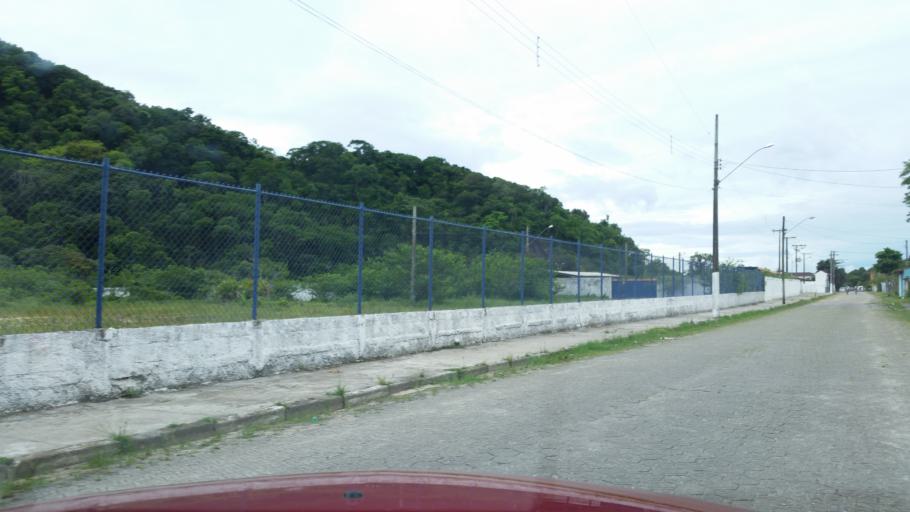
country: BR
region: Sao Paulo
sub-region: Iguape
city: Iguape
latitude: -24.7027
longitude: -47.5538
